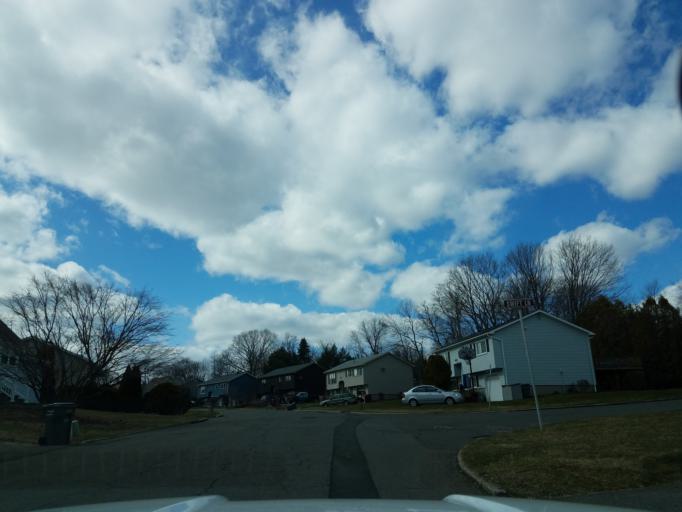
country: US
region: Connecticut
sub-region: New Haven County
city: Prospect
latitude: 41.4812
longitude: -73.0083
